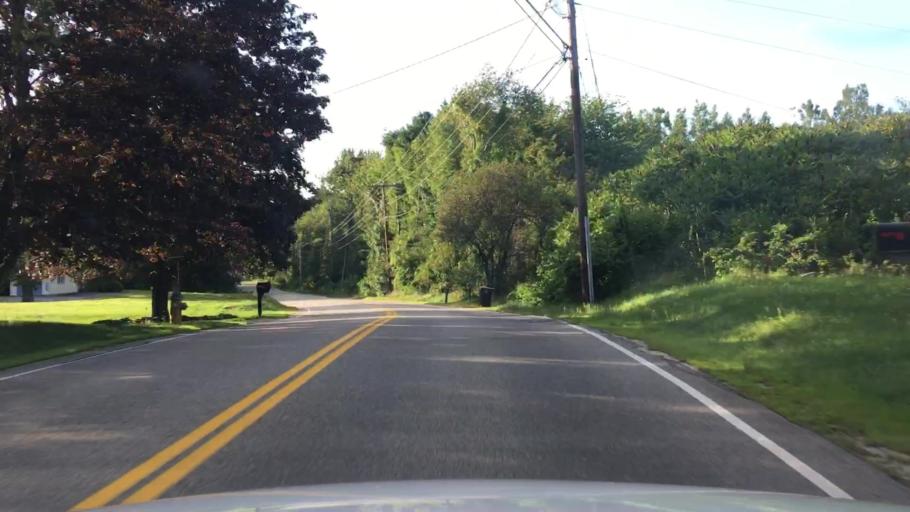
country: US
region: Maine
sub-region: Cumberland County
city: Scarborough
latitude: 43.5742
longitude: -70.2815
